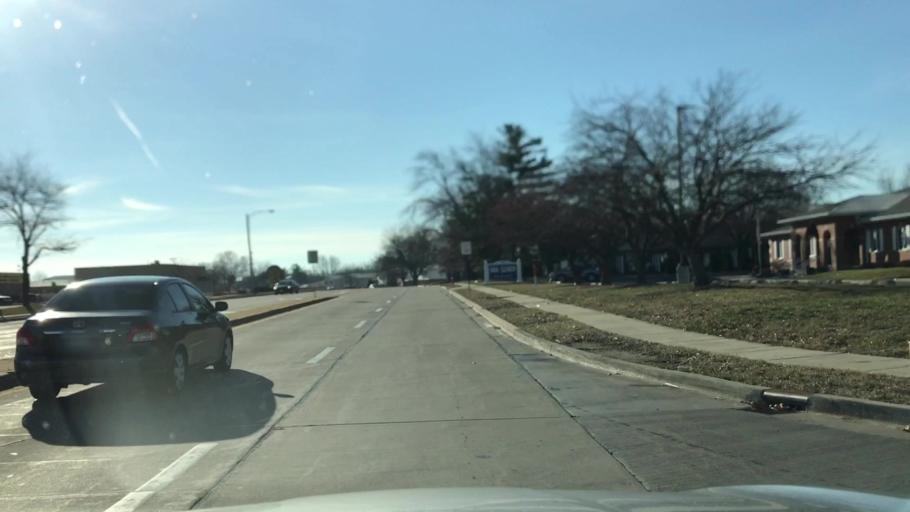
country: US
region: Illinois
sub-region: McLean County
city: Normal
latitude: 40.5102
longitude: -88.9608
